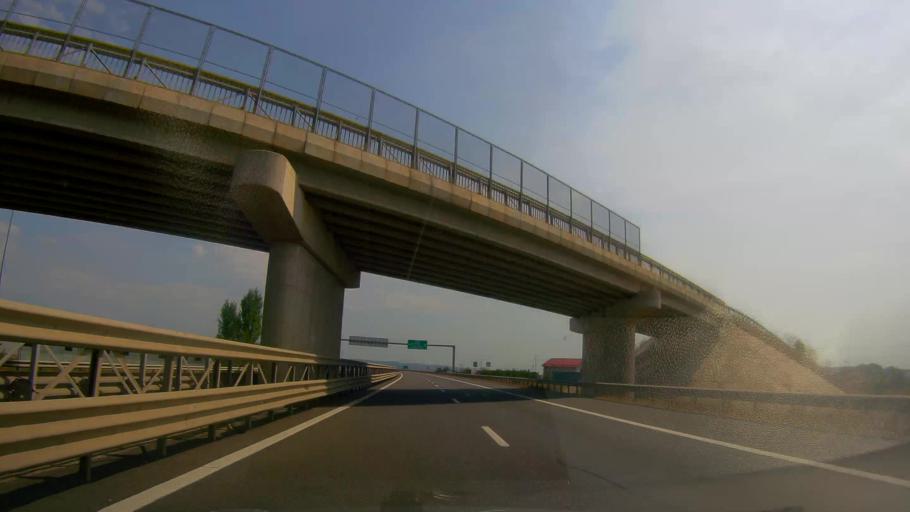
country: RO
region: Cluj
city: Turda
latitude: 46.5238
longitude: 23.8043
